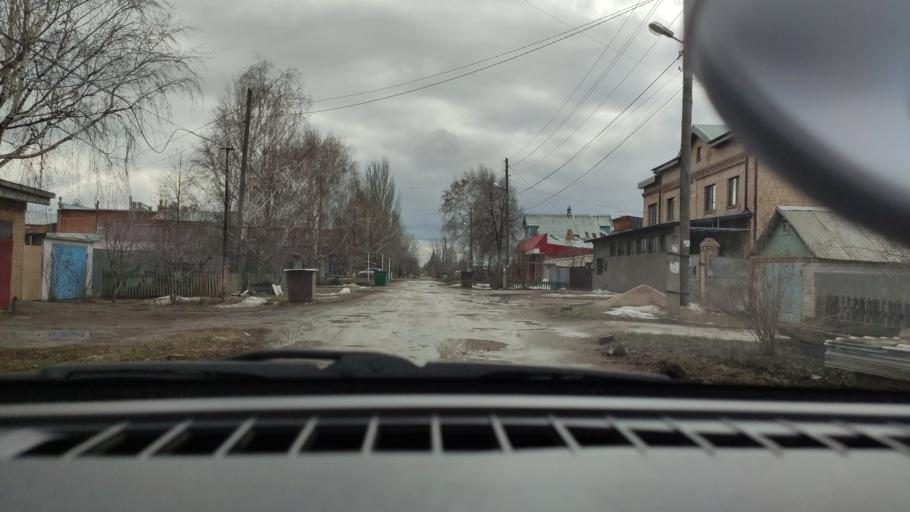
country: RU
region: Samara
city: Petra-Dubrava
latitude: 53.2514
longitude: 50.3237
